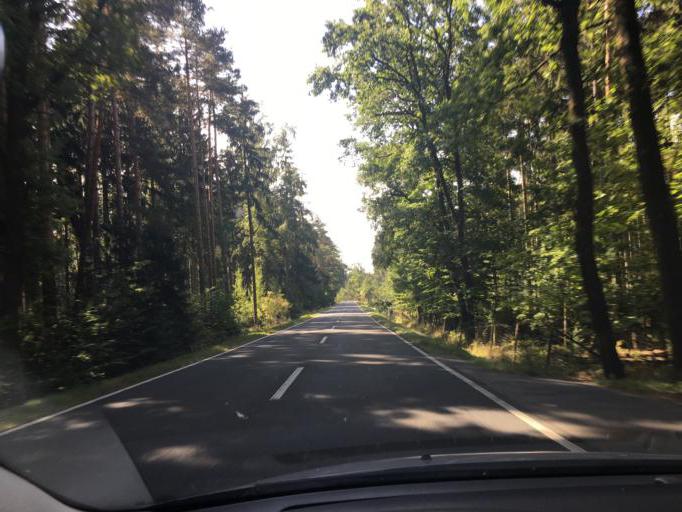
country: DE
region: Thuringia
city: Auma
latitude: 50.7191
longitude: 11.9058
